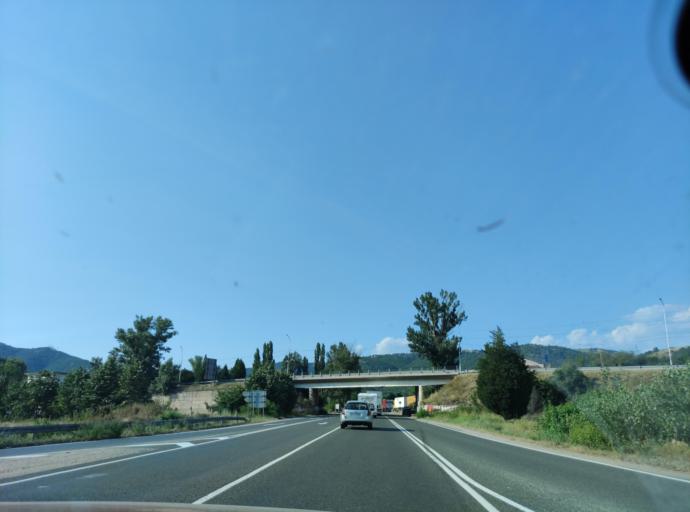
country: BG
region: Blagoevgrad
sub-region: Obshtina Simitli
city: Simitli
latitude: 41.8896
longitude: 23.1168
